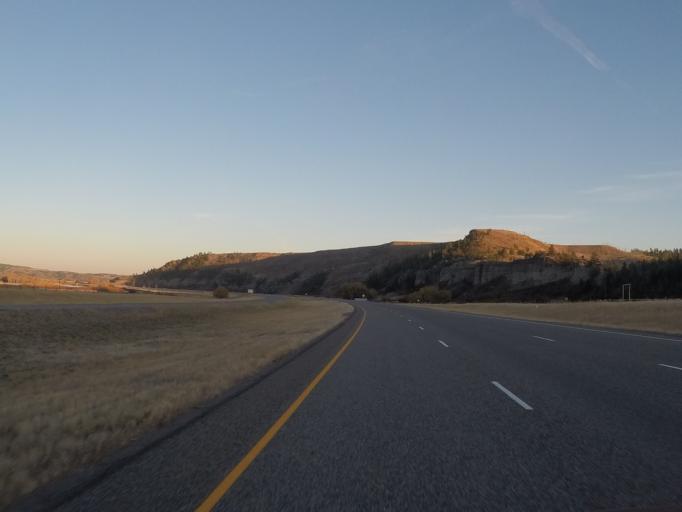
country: US
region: Montana
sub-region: Sweet Grass County
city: Big Timber
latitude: 45.7335
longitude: -109.7536
